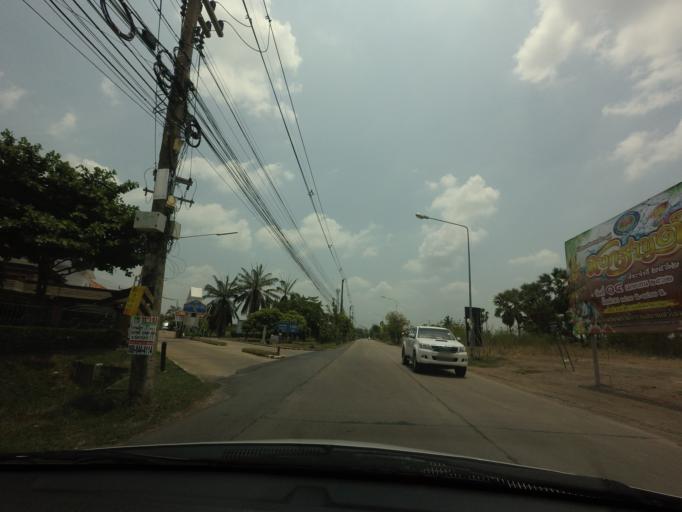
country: TH
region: Pathum Thani
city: Sam Khok
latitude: 14.0443
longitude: 100.5320
